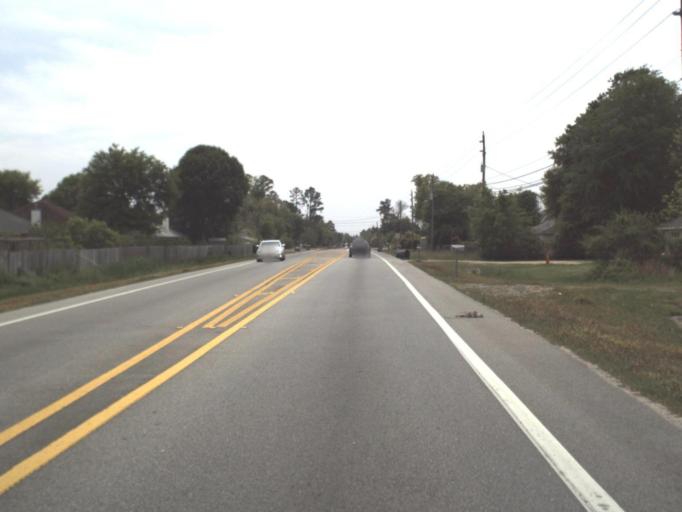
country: US
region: Florida
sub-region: Escambia County
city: Bellview
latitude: 30.4714
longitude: -87.3239
